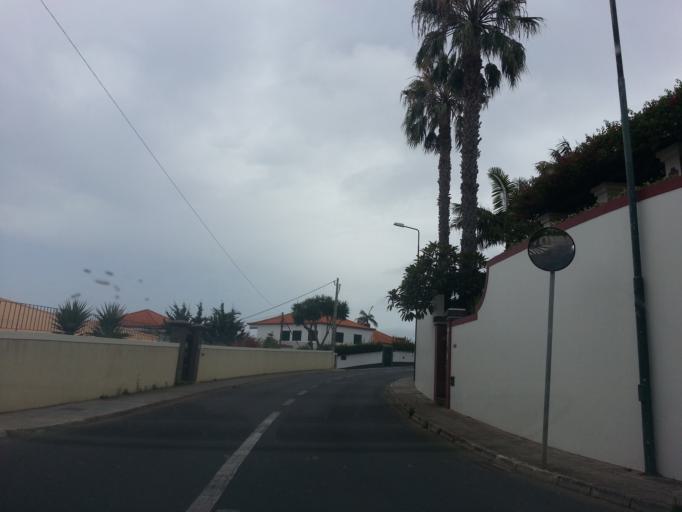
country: PT
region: Madeira
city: Camara de Lobos
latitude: 32.6520
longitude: -16.9346
